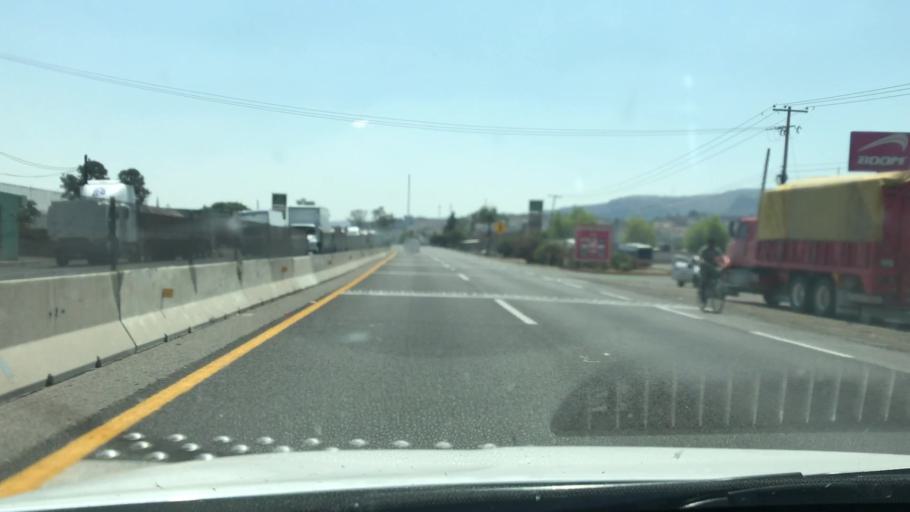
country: MX
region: Guanajuato
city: Abasolo
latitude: 20.4506
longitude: -101.5541
